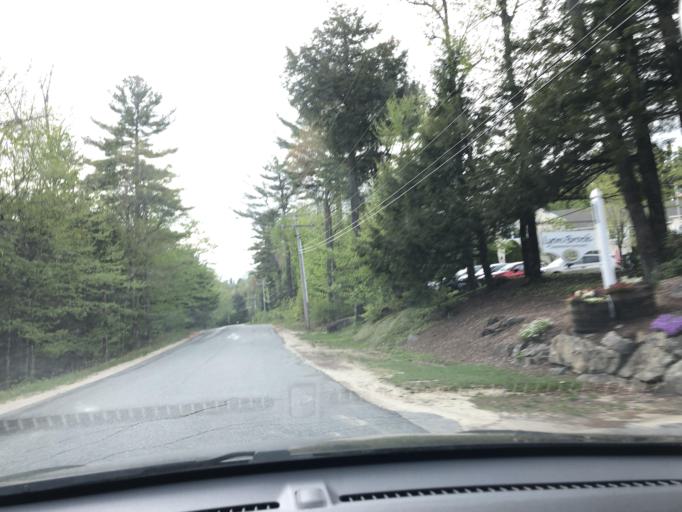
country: US
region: New Hampshire
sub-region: Merrimack County
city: New London
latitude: 43.4174
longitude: -72.0007
